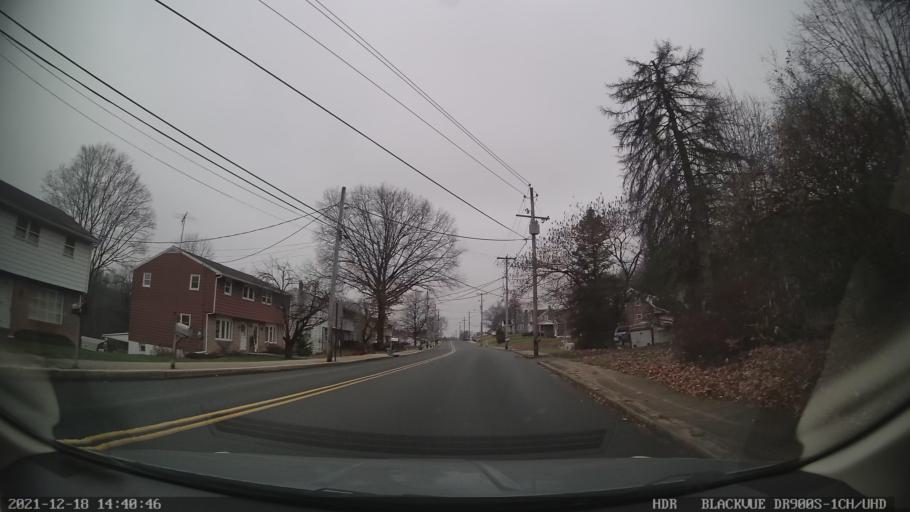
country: US
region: Pennsylvania
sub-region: Berks County
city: New Berlinville
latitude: 40.3671
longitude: -75.6291
